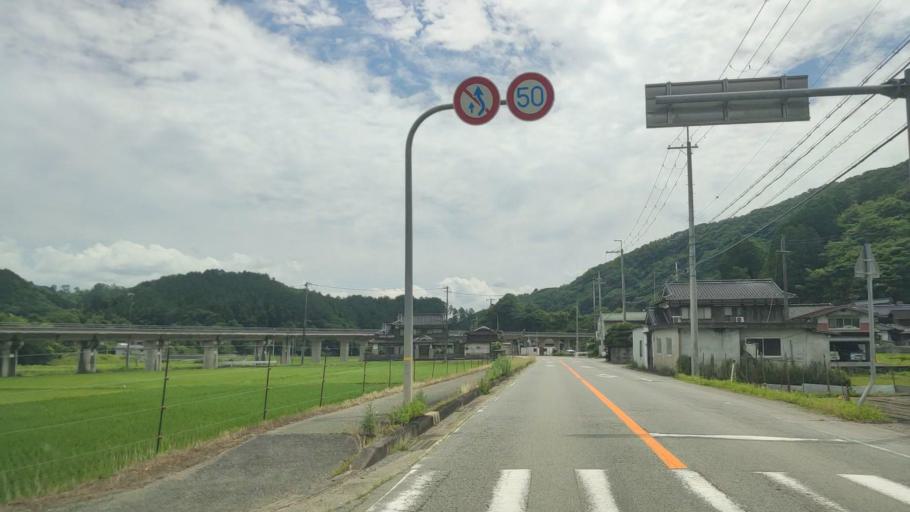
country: JP
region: Hyogo
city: Yamazakicho-nakabirose
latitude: 35.0368
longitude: 134.3677
